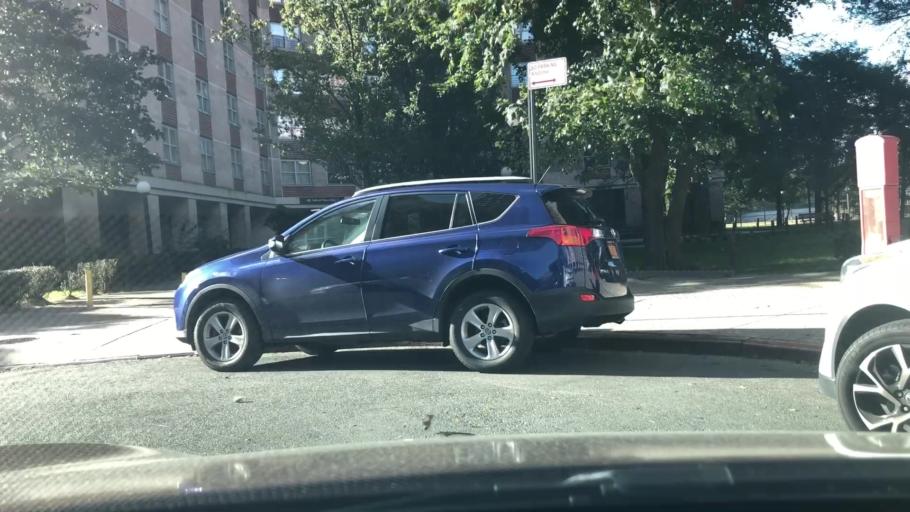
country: US
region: New York
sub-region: Bronx
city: Eastchester
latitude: 40.8755
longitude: -73.8285
